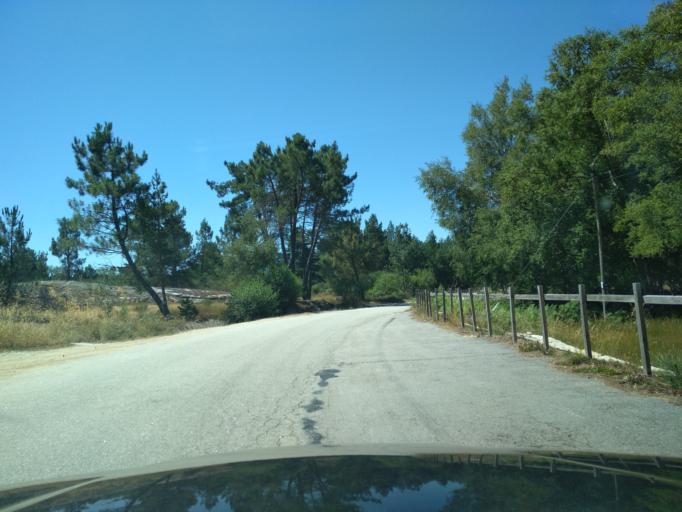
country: PT
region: Vila Real
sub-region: Vila Pouca de Aguiar
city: Vila Pouca de Aguiar
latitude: 41.5041
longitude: -7.6635
